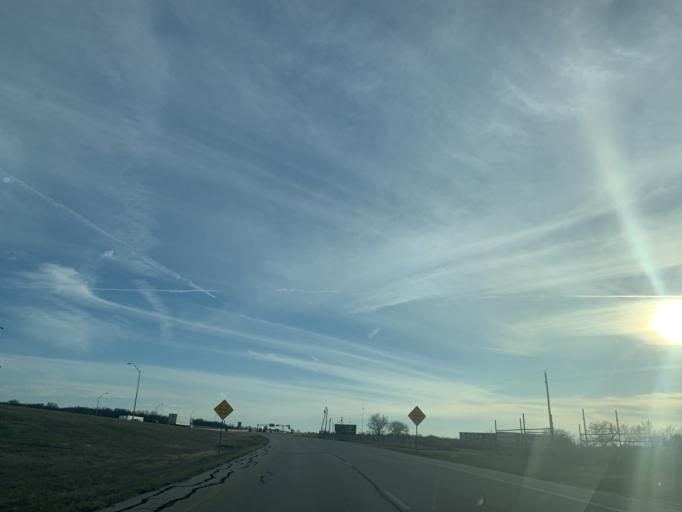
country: US
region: Texas
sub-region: Bell County
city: Salado
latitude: 30.8742
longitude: -97.5820
